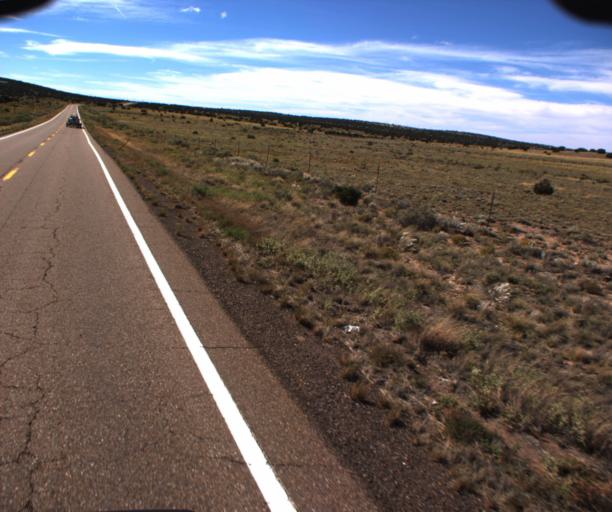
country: US
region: Arizona
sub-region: Apache County
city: Saint Johns
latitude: 34.4871
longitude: -109.5326
